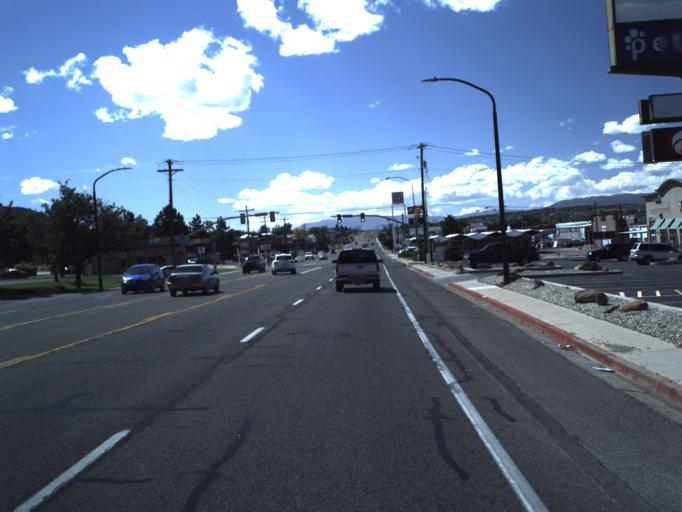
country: US
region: Utah
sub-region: Iron County
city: Cedar City
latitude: 37.6666
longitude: -113.0635
